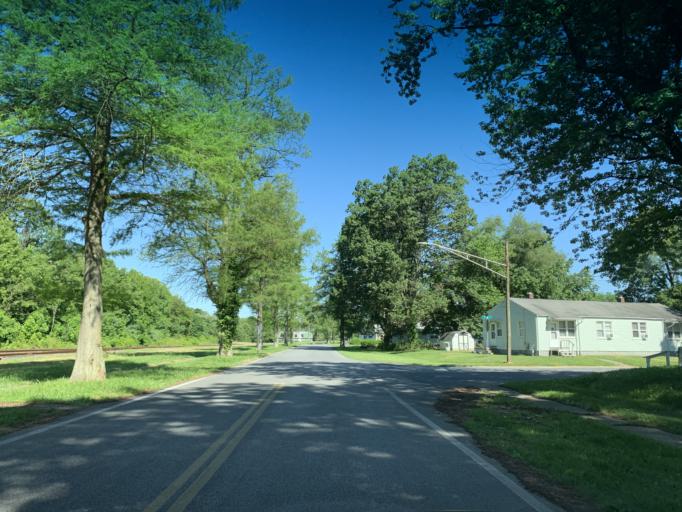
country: US
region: Maryland
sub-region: Harford County
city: Aberdeen
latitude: 39.5006
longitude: -76.1623
